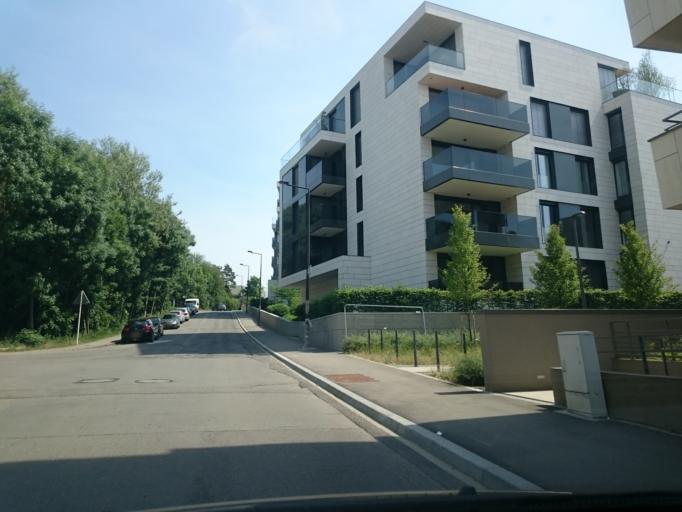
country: LU
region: Luxembourg
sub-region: Canton de Luxembourg
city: Luxembourg
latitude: 49.6040
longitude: 6.1054
